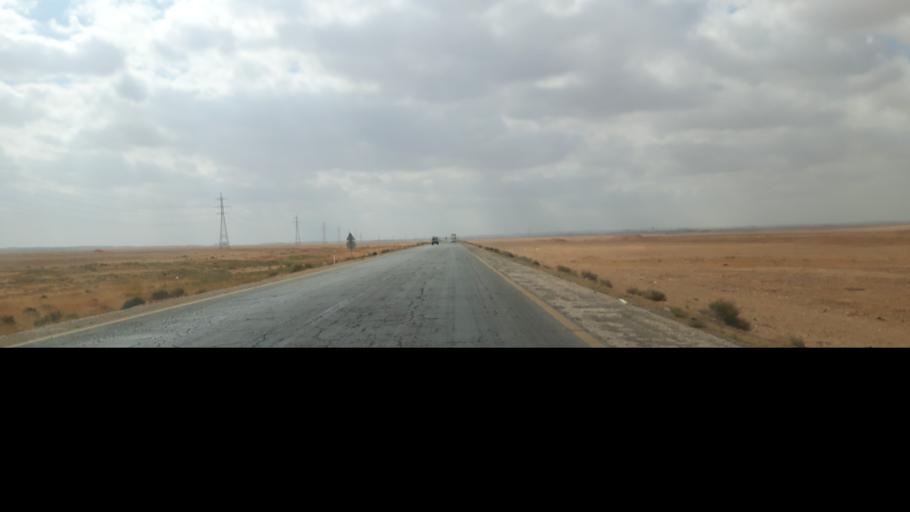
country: JO
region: Amman
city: Sahab
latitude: 31.7619
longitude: 36.3030
